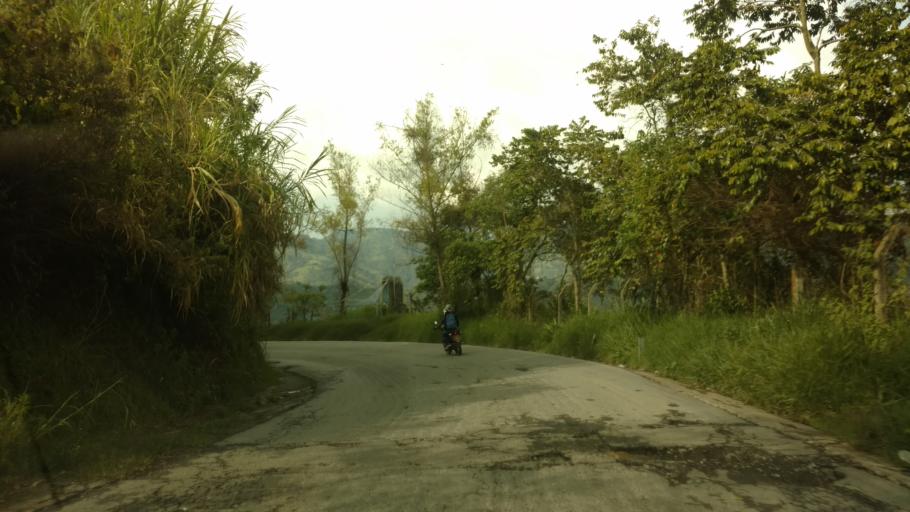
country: CO
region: Caldas
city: Neira
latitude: 5.1719
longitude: -75.5194
